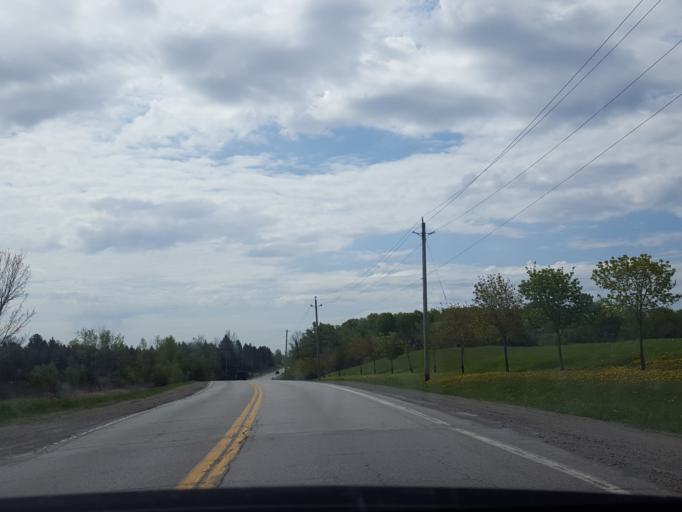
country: CA
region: Ontario
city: Oshawa
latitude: 43.9501
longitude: -78.7198
